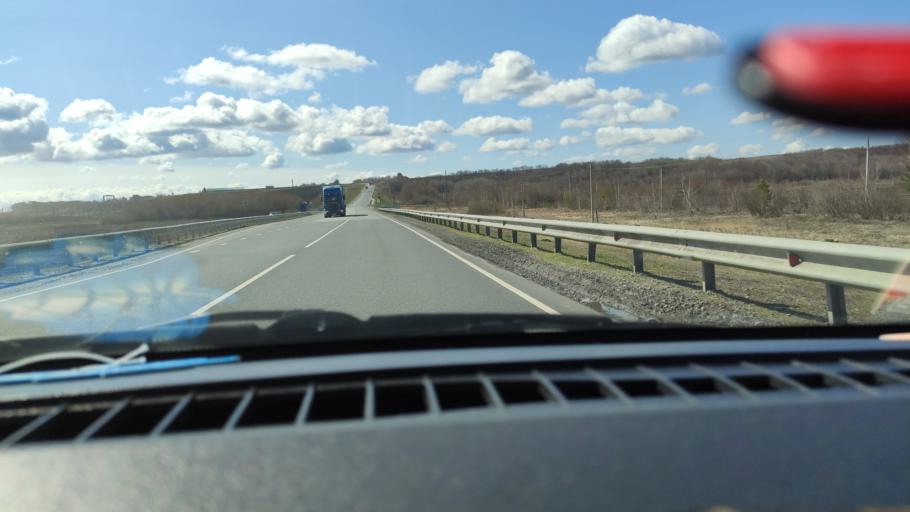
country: RU
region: Samara
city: Syzran'
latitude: 52.9664
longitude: 48.3074
